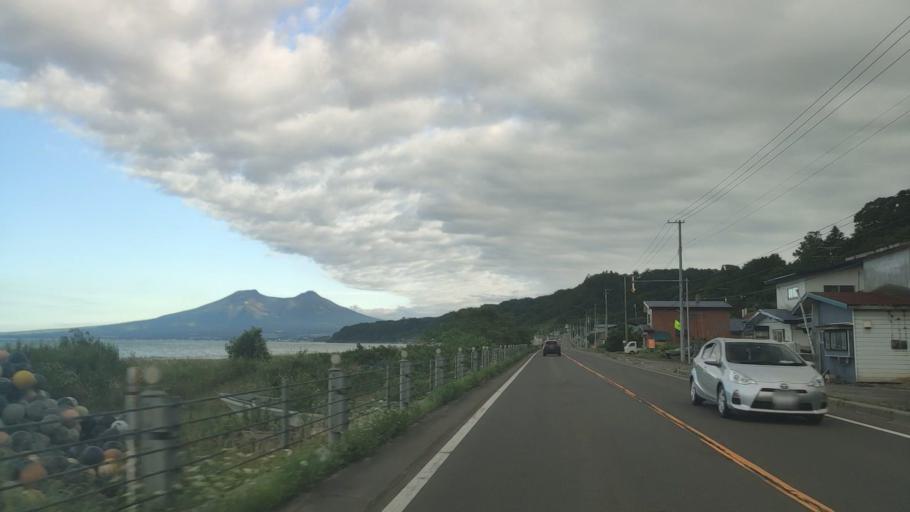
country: JP
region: Hokkaido
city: Nanae
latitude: 42.1323
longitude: 140.5104
